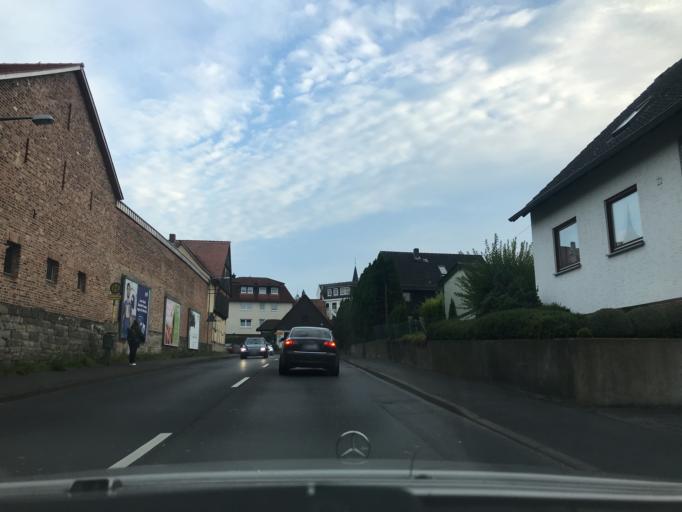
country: DE
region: Hesse
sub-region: Regierungsbezirk Kassel
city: Vellmar
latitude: 51.3383
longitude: 9.4382
